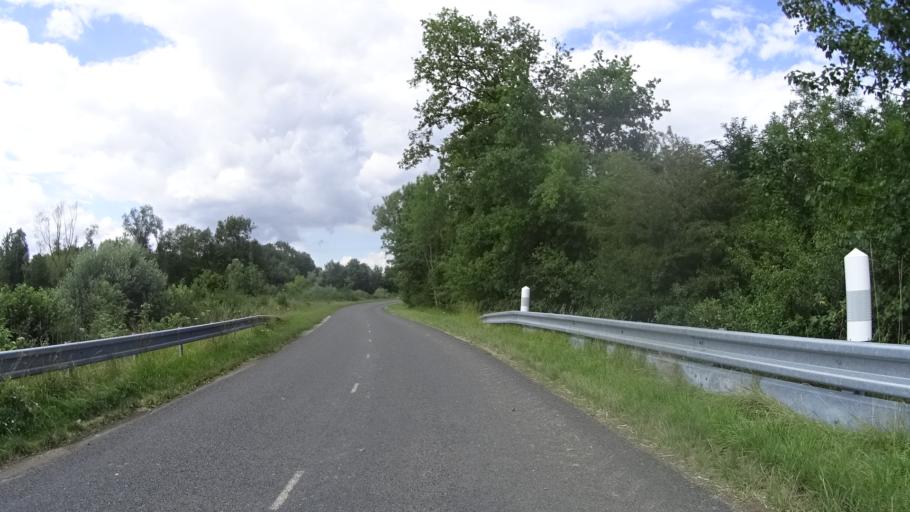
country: FR
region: Champagne-Ardenne
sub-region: Departement de la Haute-Marne
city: Villiers-en-Lieu
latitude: 48.6381
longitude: 4.8381
